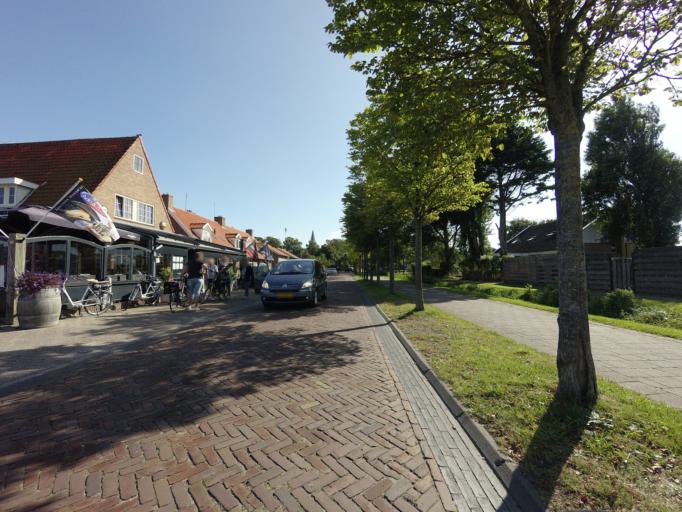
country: NL
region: Friesland
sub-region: Gemeente Terschelling
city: West-Terschelling
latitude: 53.3848
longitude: 5.2847
